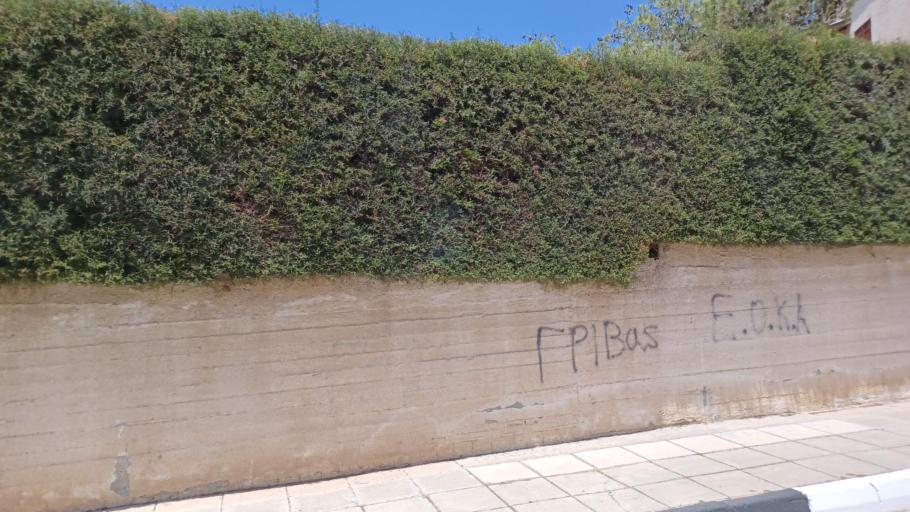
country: CY
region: Larnaka
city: Troulloi
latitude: 35.0343
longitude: 33.6157
